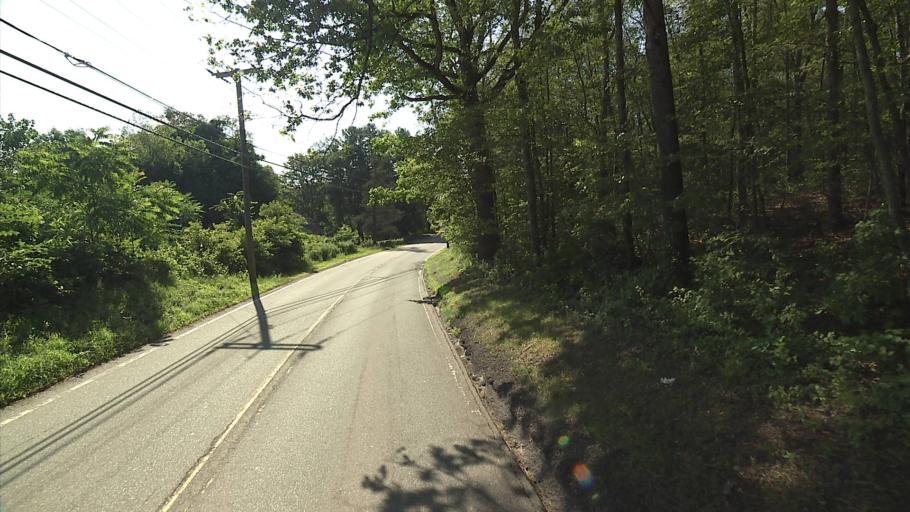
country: US
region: Connecticut
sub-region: New London County
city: Montville Center
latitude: 41.4631
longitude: -72.1558
